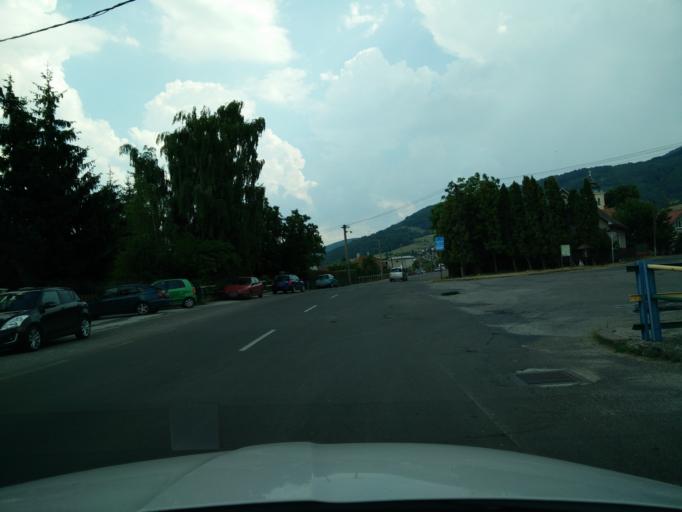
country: SK
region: Nitriansky
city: Novaky
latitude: 48.7971
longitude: 18.4779
